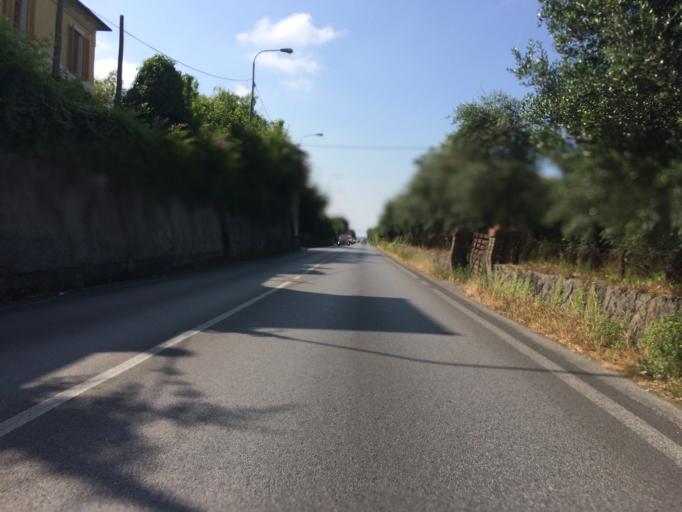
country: IT
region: Tuscany
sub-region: Provincia di Massa-Carrara
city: Capanne-Prato-Cinquale
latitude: 44.0119
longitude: 10.1583
